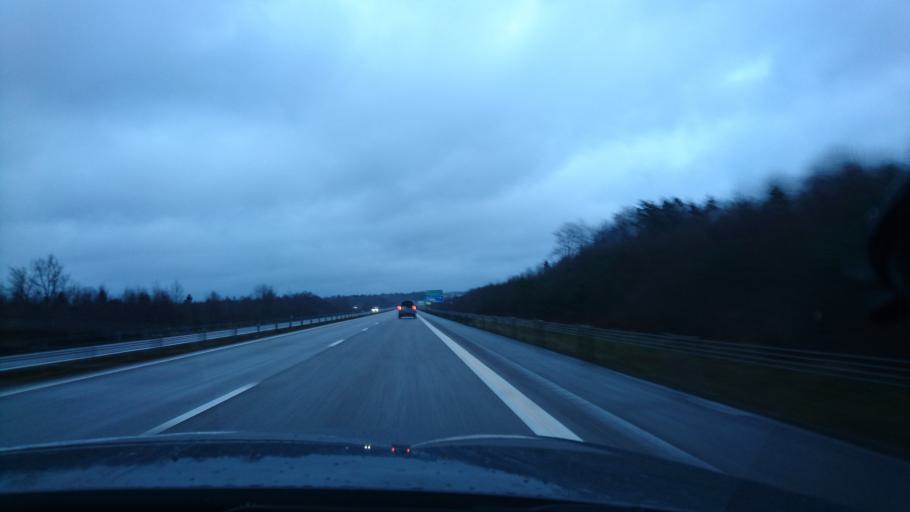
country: SE
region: Kronoberg
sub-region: Markaryds Kommun
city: Markaryd
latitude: 56.4373
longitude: 13.5809
